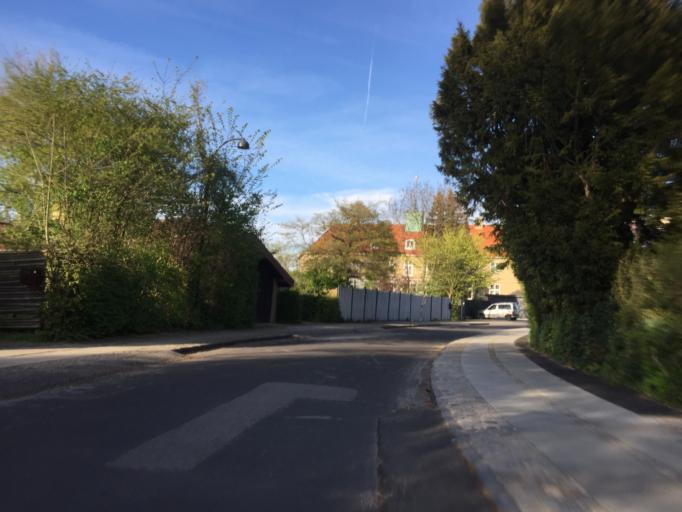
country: DK
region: Capital Region
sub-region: Frederiksberg Kommune
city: Frederiksberg
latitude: 55.7251
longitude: 12.5510
